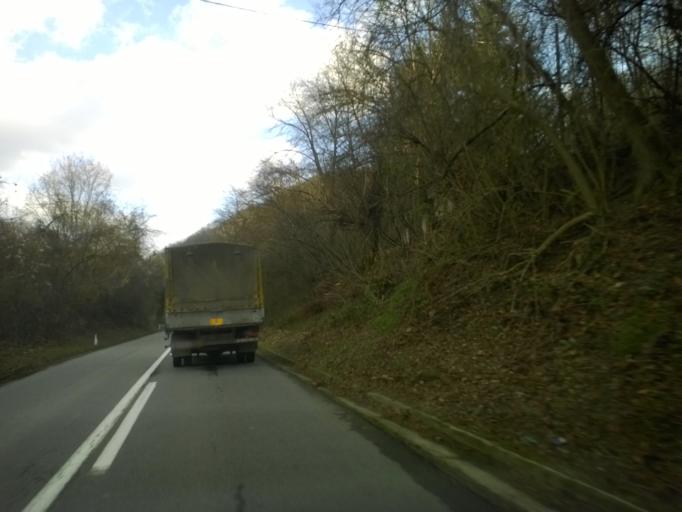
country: RO
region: Caras-Severin
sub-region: Comuna Berzasca
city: Liubcova
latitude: 44.6467
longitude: 21.8544
